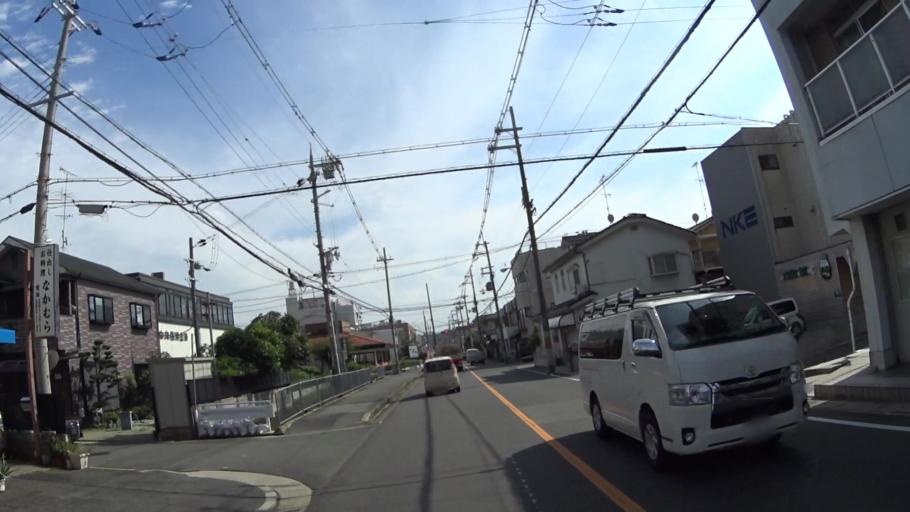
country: JP
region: Kyoto
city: Muko
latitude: 34.9710
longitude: 135.6941
